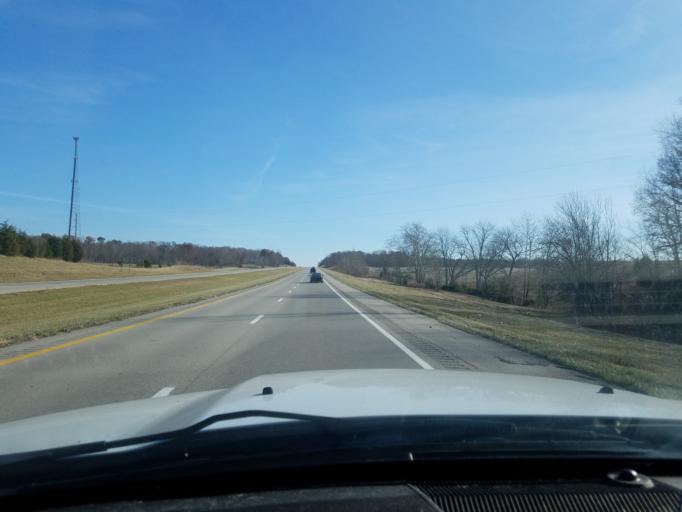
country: US
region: Ohio
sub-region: Adams County
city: Winchester
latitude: 38.9338
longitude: -83.6198
